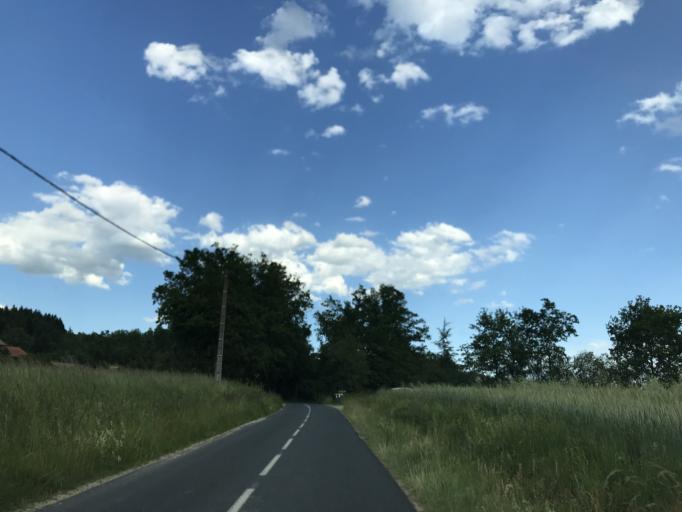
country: FR
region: Auvergne
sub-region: Departement du Puy-de-Dome
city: Courpiere
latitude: 45.7721
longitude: 3.5969
